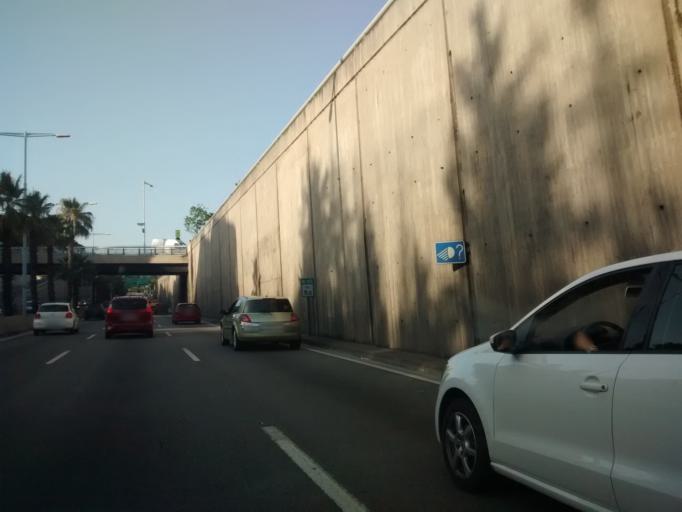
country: ES
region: Catalonia
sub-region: Provincia de Barcelona
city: Esplugues de Llobregat
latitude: 41.3890
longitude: 2.1073
